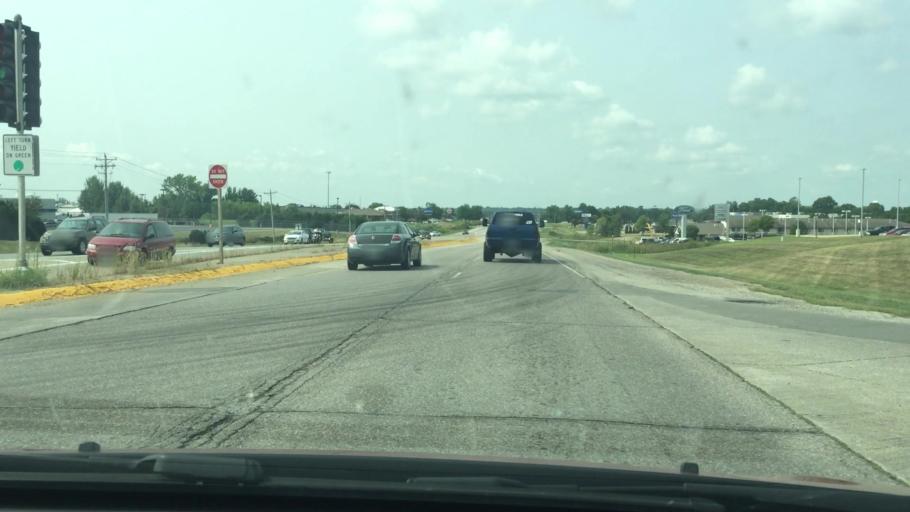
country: US
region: Iowa
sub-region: Muscatine County
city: Muscatine
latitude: 41.4594
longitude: -91.0178
